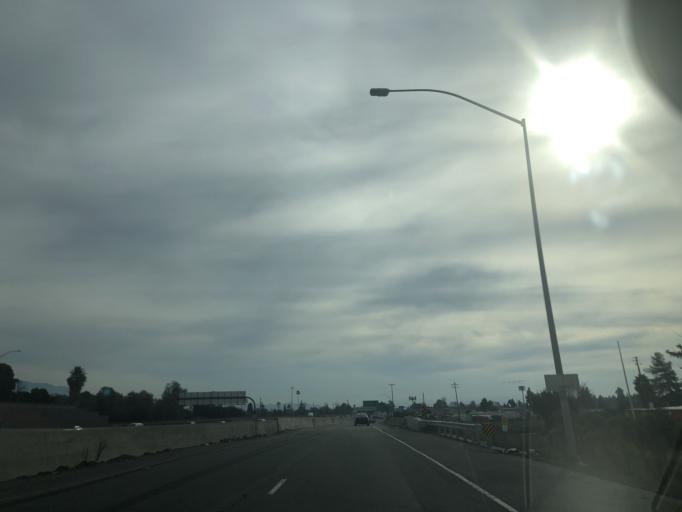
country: US
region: California
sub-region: Contra Costa County
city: Pacheco
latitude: 37.9915
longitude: -122.0683
